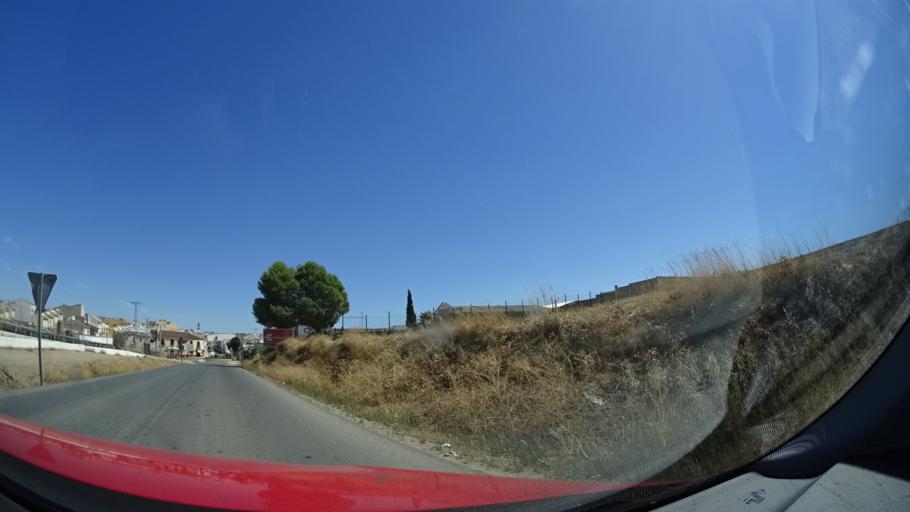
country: ES
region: Andalusia
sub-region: Provincia de Malaga
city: Sierra de Yeguas
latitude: 37.1241
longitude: -4.8752
